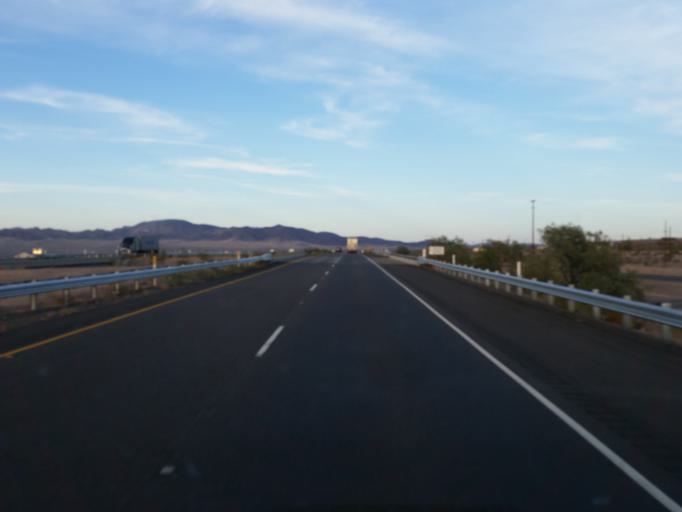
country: US
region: California
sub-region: San Bernardino County
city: Twentynine Palms
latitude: 34.7252
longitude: -116.1642
